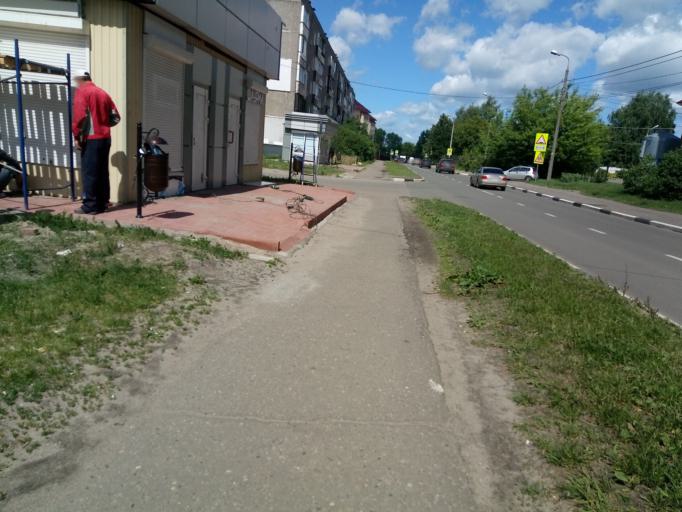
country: RU
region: Jaroslavl
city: Yaroslavl
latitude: 57.6562
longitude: 39.9580
